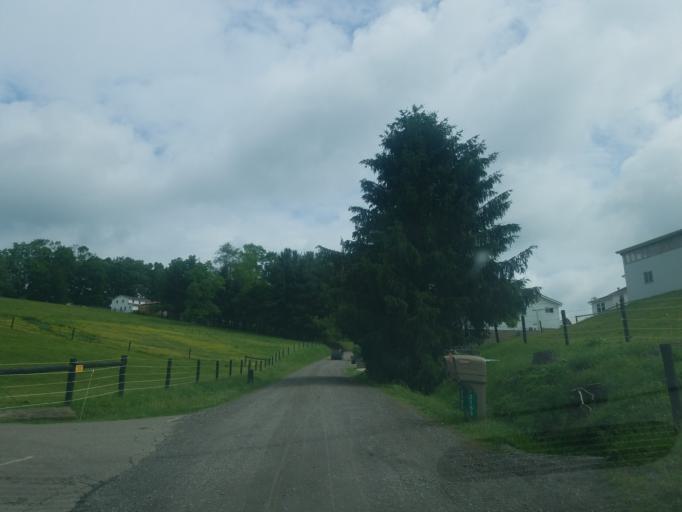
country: US
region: Ohio
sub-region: Holmes County
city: Millersburg
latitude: 40.4688
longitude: -81.8026
